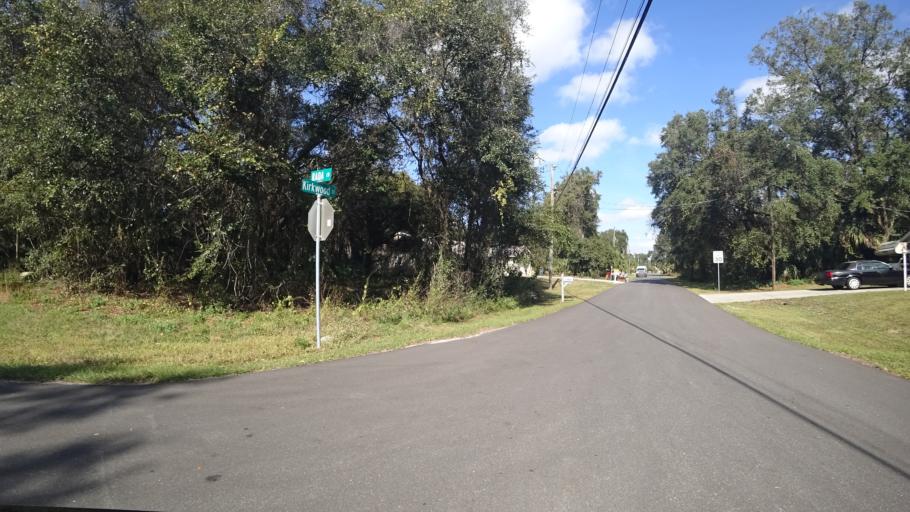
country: US
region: Florida
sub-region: Charlotte County
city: Port Charlotte
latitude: 27.0594
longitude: -82.1175
